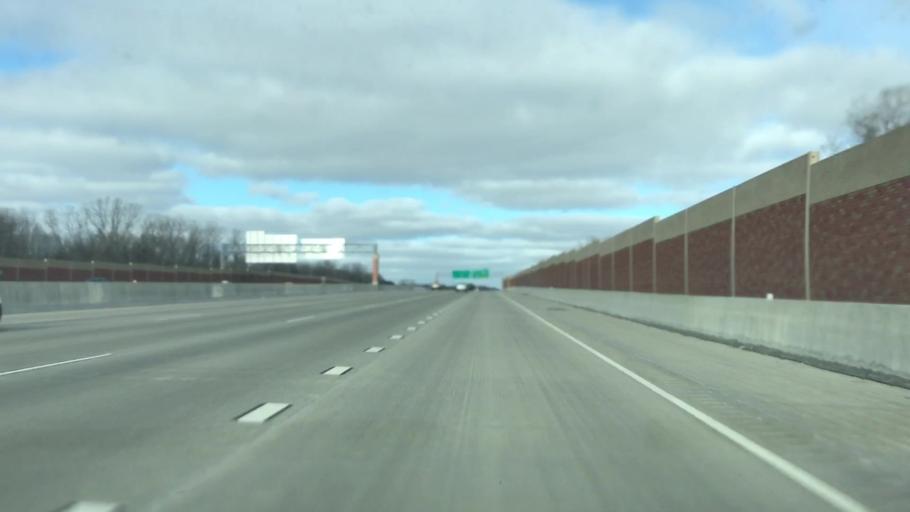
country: US
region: Wisconsin
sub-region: Brown County
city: Ashwaubenon
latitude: 44.5008
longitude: -88.0817
